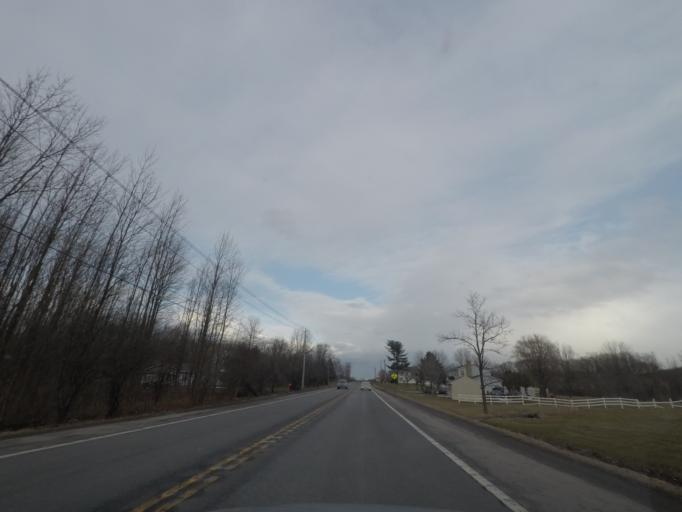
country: US
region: New York
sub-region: Oneida County
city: Vernon
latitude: 43.0745
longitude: -75.4654
